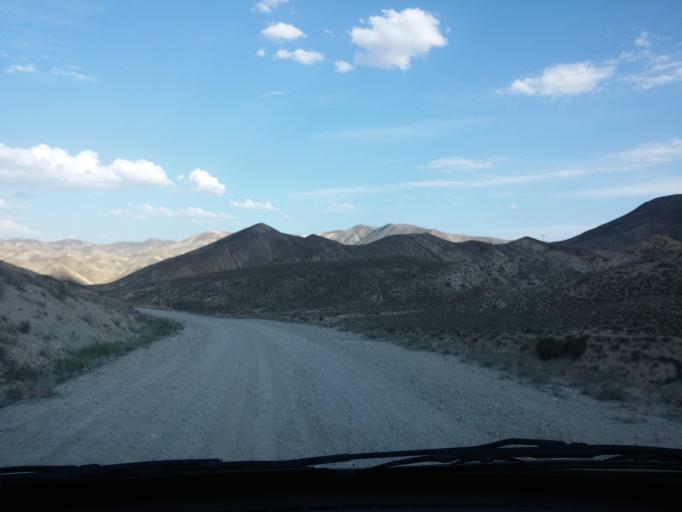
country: IR
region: Tehran
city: Damavand
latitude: 35.5370
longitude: 52.2183
